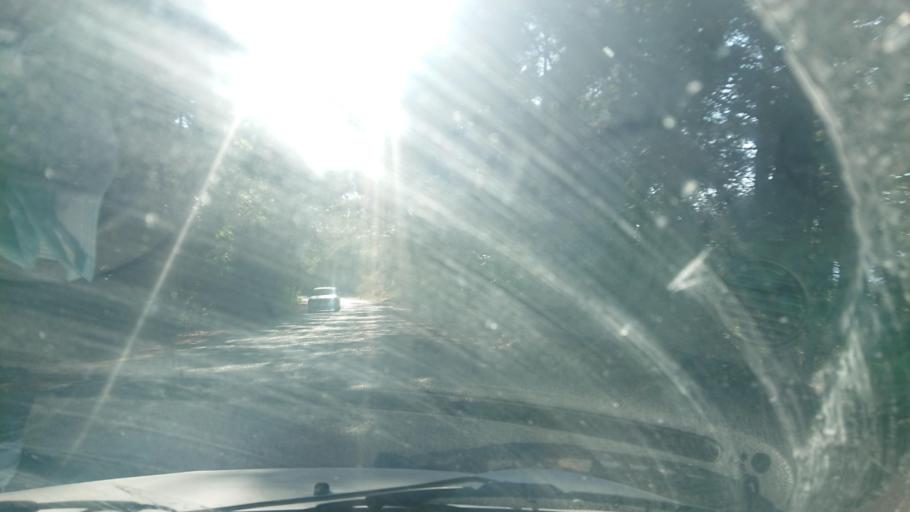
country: TR
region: Aydin
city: Atburgazi
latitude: 37.6908
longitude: 27.1464
